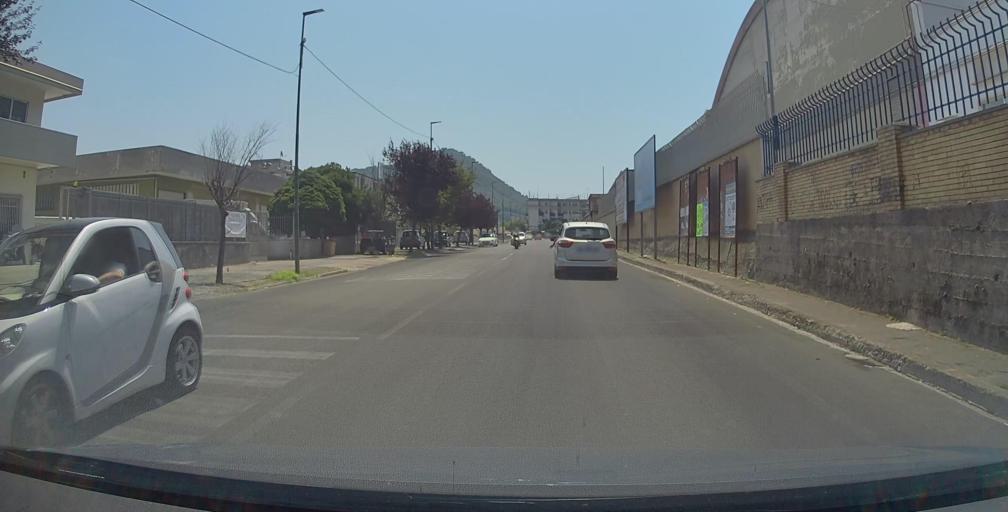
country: IT
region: Campania
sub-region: Provincia di Salerno
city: Cava De Tirreni
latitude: 40.7143
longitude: 14.6979
